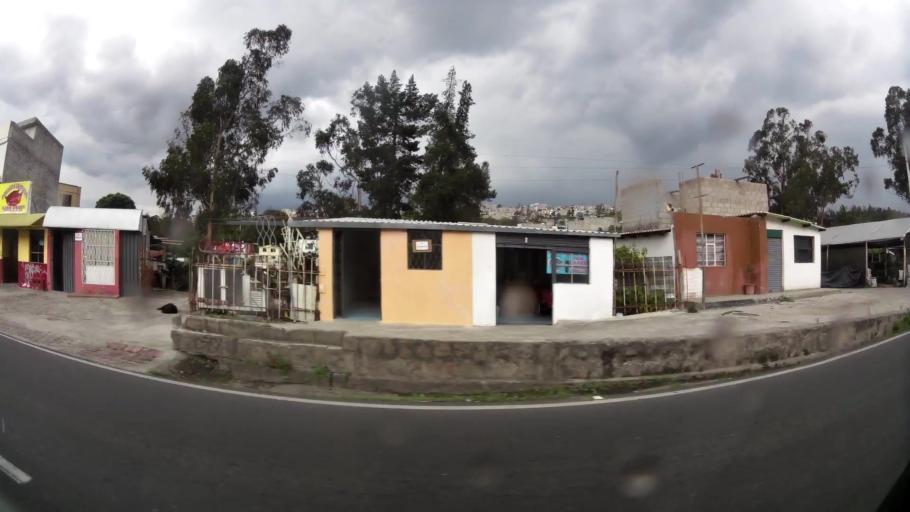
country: EC
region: Pichincha
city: Quito
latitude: -0.0740
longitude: -78.4790
